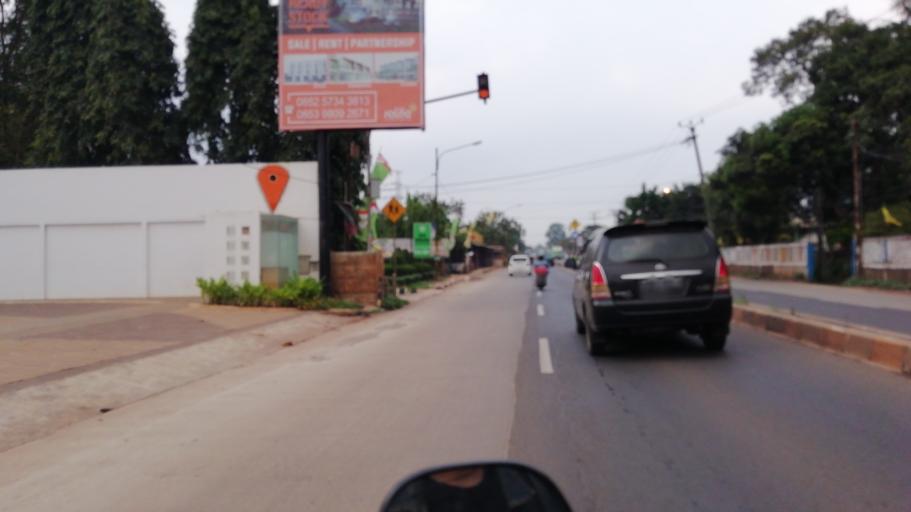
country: ID
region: West Java
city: Parung
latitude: -6.4521
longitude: 106.7314
